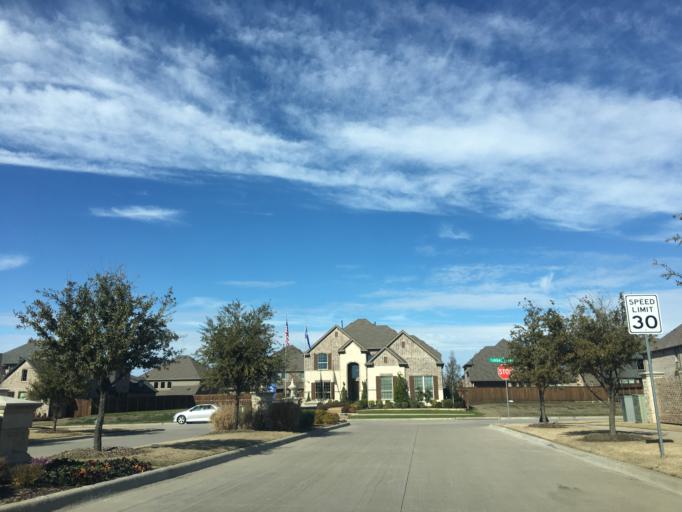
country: US
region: Texas
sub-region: Denton County
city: Little Elm
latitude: 33.2117
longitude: -96.8909
